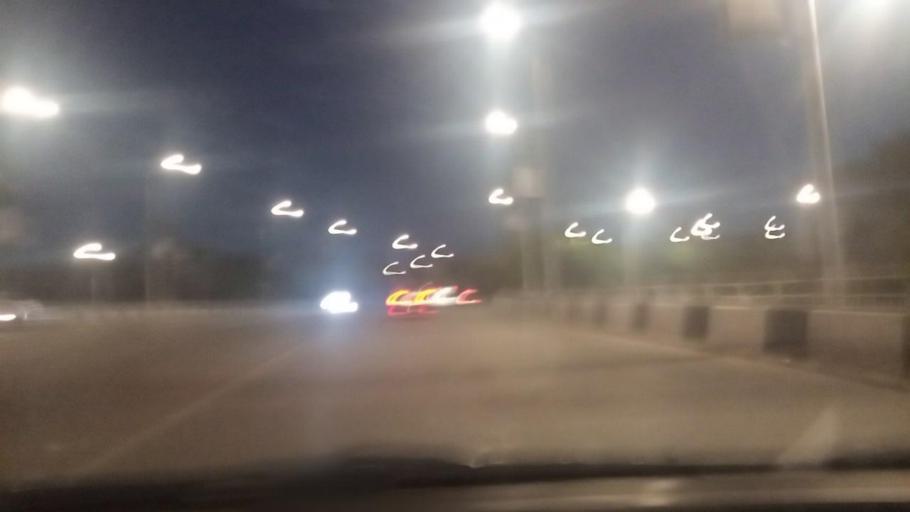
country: UZ
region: Toshkent Shahri
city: Tashkent
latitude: 41.2608
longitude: 69.2269
